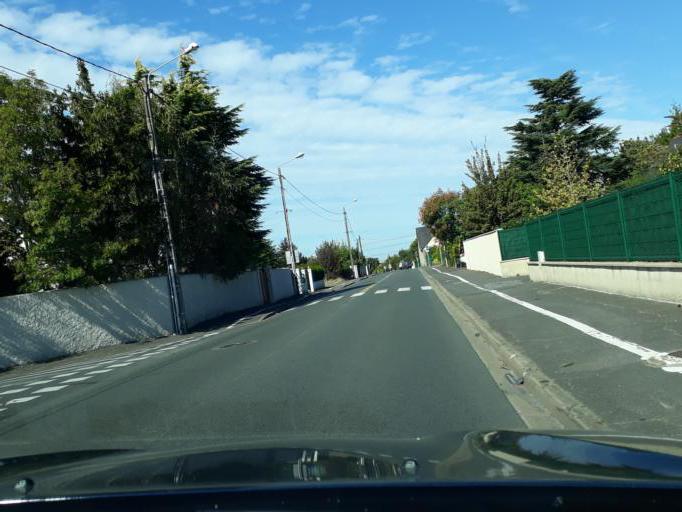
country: FR
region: Centre
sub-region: Departement d'Indre-et-Loire
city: Saint-Avertin
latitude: 47.3453
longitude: 0.7354
